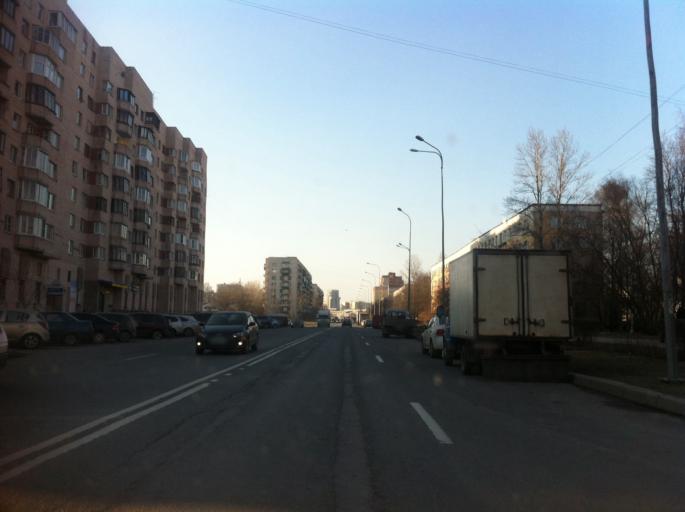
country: RU
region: St.-Petersburg
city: Dachnoye
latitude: 59.8423
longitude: 30.2351
